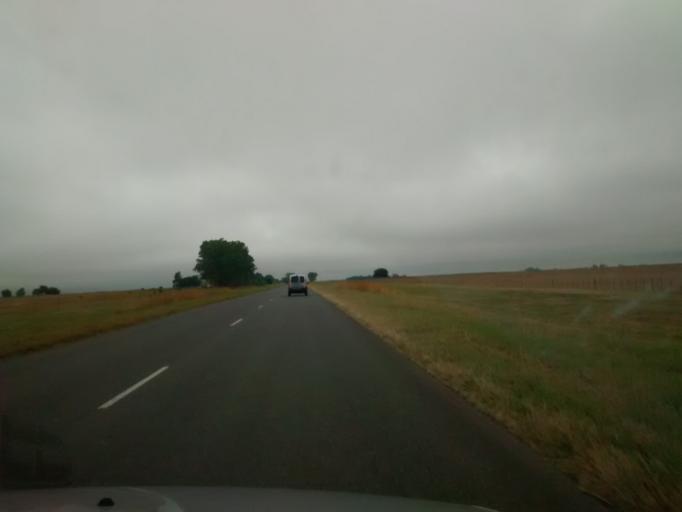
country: AR
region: Buenos Aires
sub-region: Partido de Ayacucho
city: Ayacucho
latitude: -37.2373
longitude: -58.4918
